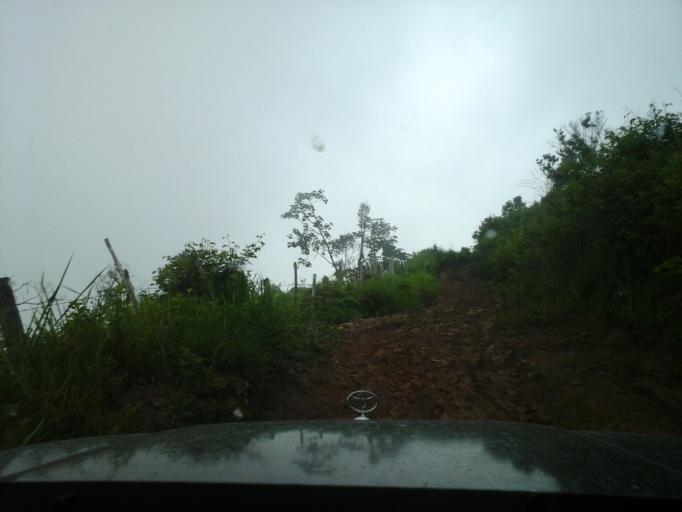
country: CO
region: Cesar
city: Agustin Codazzi
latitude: 9.9595
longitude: -73.0618
